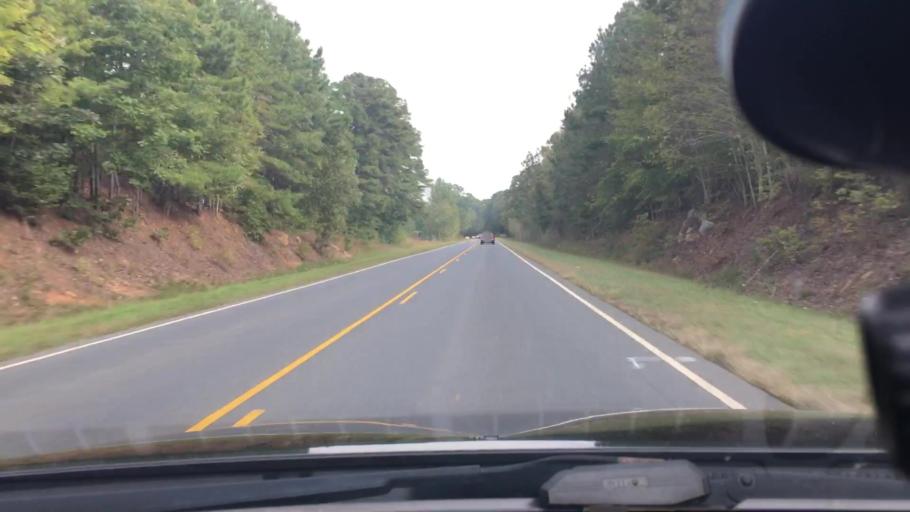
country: US
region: North Carolina
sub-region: Montgomery County
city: Mount Gilead
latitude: 35.3061
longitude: -80.0364
